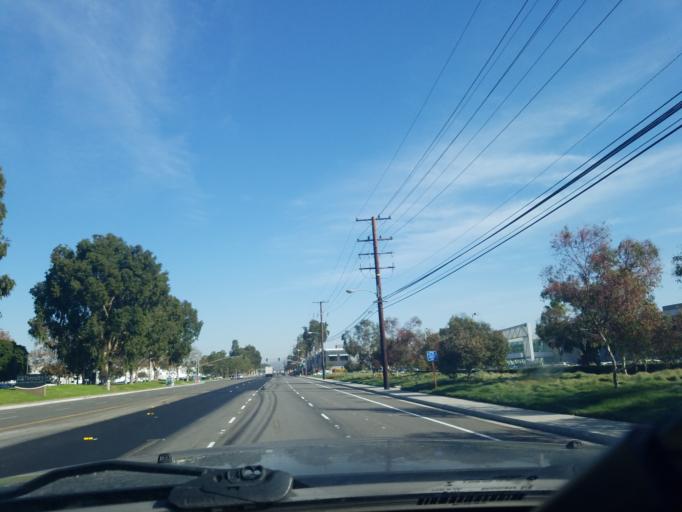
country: US
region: California
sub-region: Orange County
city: Irvine
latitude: 33.6987
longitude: -117.8500
